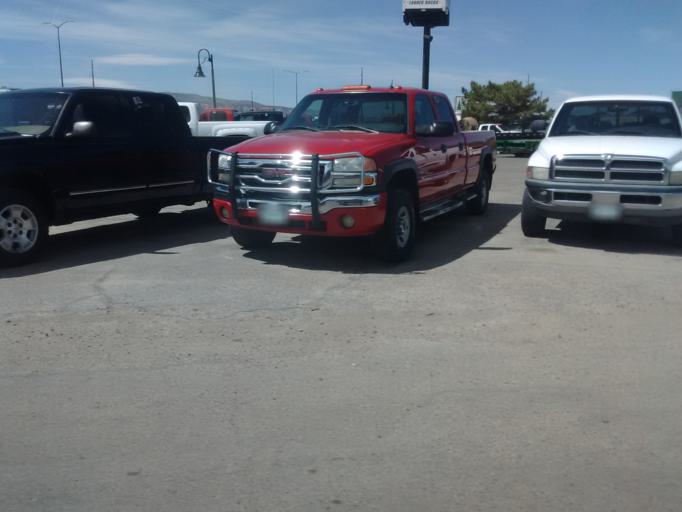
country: US
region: Colorado
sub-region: Mesa County
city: Grand Junction
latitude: 39.0819
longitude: -108.5853
